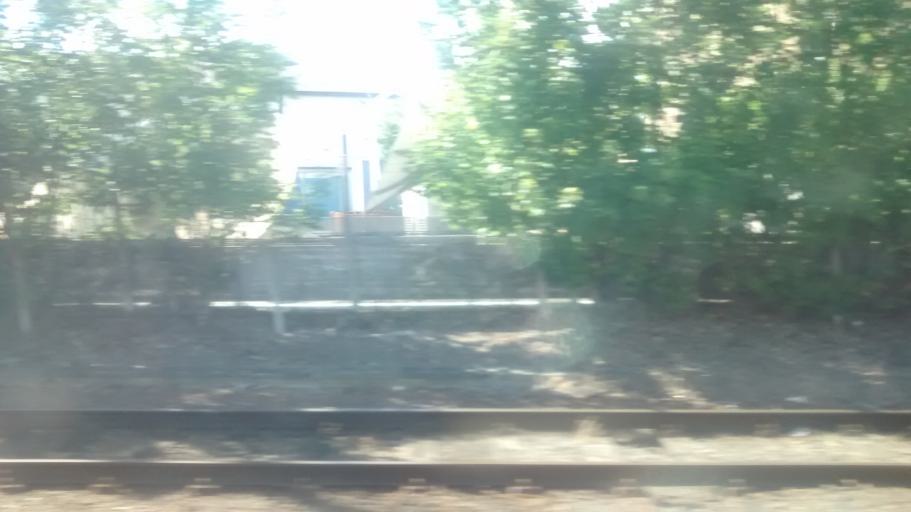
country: GB
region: England
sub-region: Cambridgeshire
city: Cambridge
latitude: 52.2020
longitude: 0.1433
